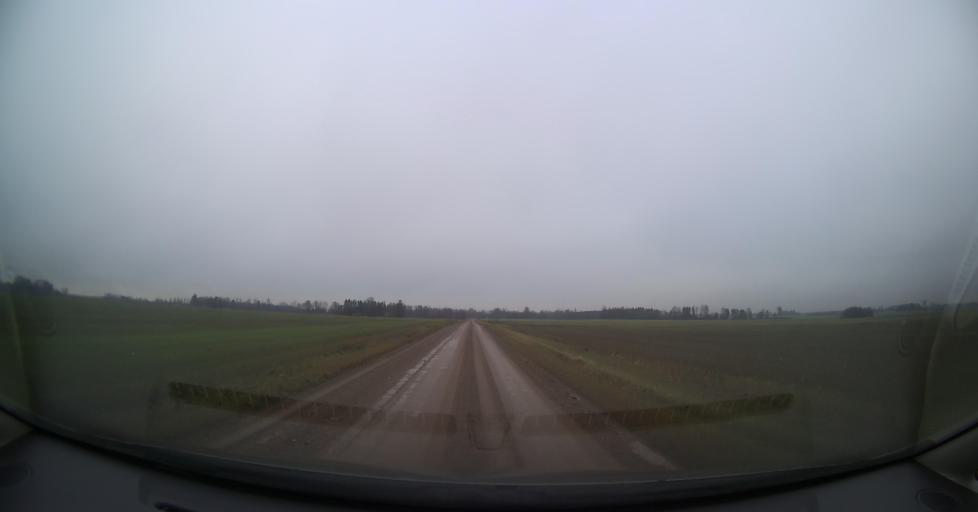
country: EE
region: Tartu
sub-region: Tartu linn
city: Tartu
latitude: 58.3851
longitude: 26.9272
